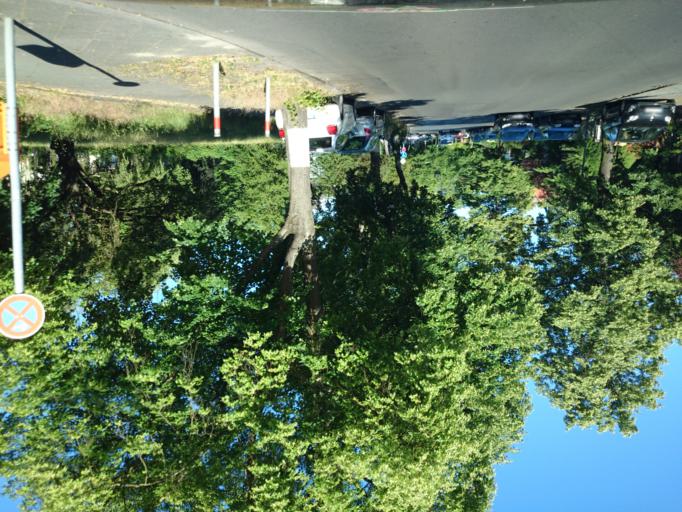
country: DE
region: Berlin
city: Lichterfelde
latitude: 52.4436
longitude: 13.3198
